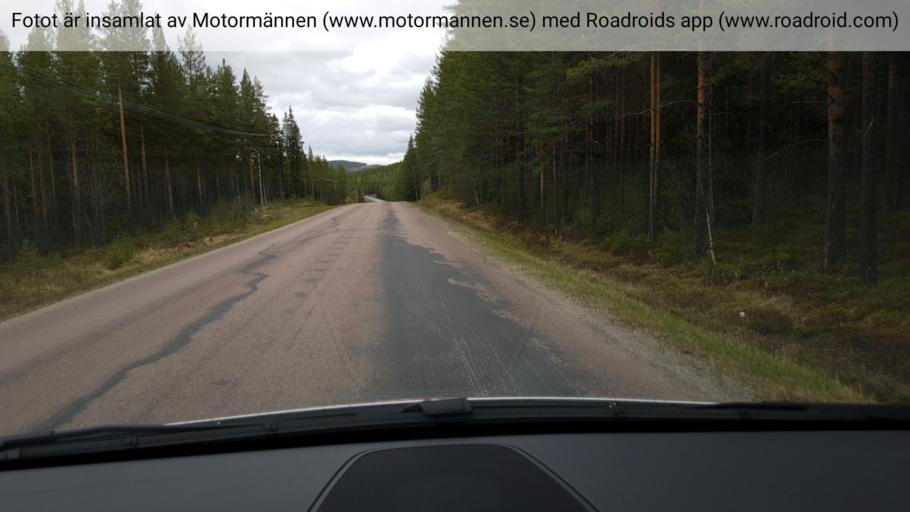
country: SE
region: Jaemtland
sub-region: Braecke Kommun
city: Braecke
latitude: 62.8364
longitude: 15.4668
